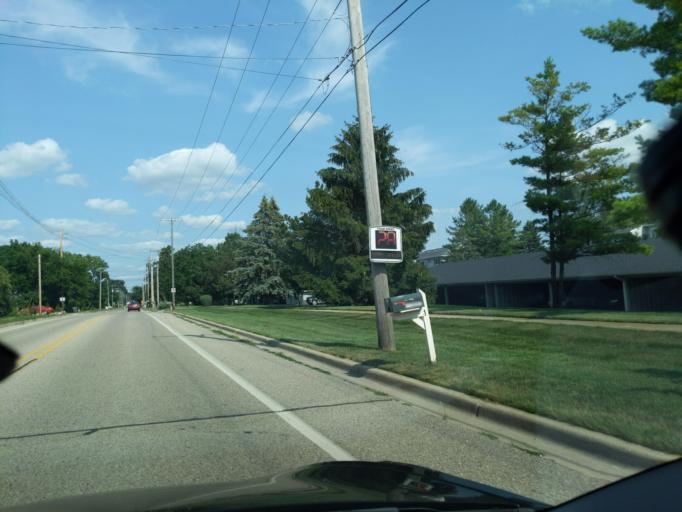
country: US
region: Michigan
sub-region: Kent County
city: Lowell
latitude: 42.9292
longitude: -85.3525
